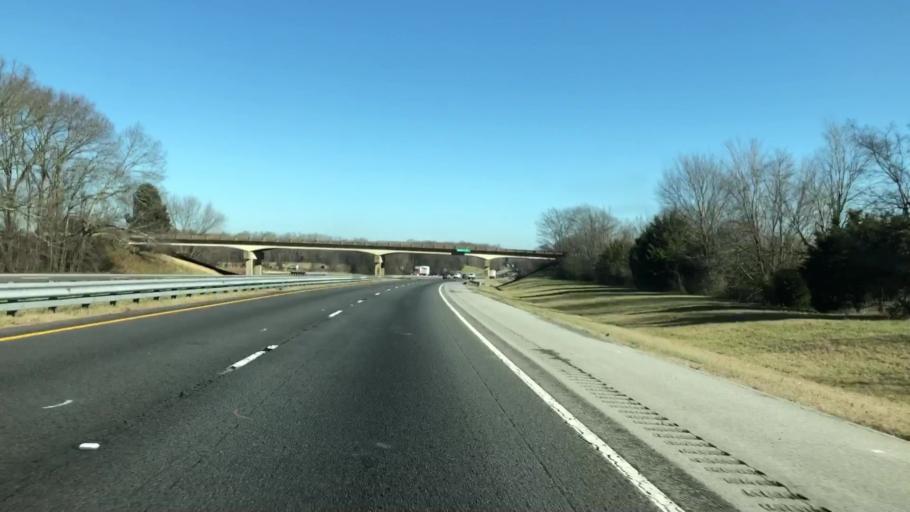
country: US
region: Alabama
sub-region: Limestone County
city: Athens
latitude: 34.8897
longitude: -86.9157
